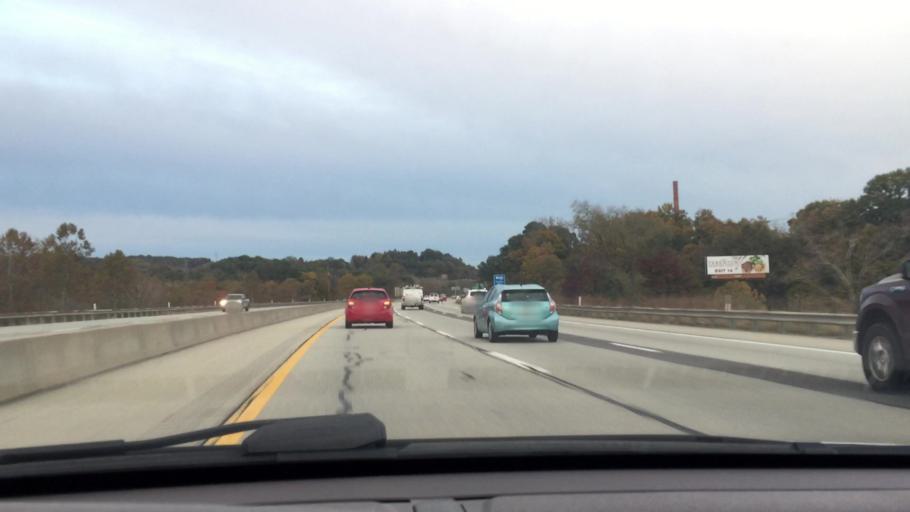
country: US
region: Pennsylvania
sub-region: Allegheny County
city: Oakmont
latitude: 40.5454
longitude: -79.8339
